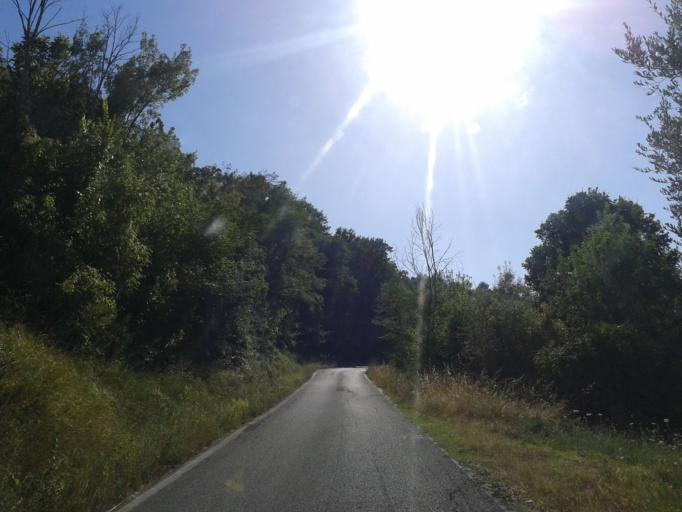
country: IT
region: Tuscany
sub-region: Province of Pisa
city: Chianni
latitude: 43.4567
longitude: 10.6317
